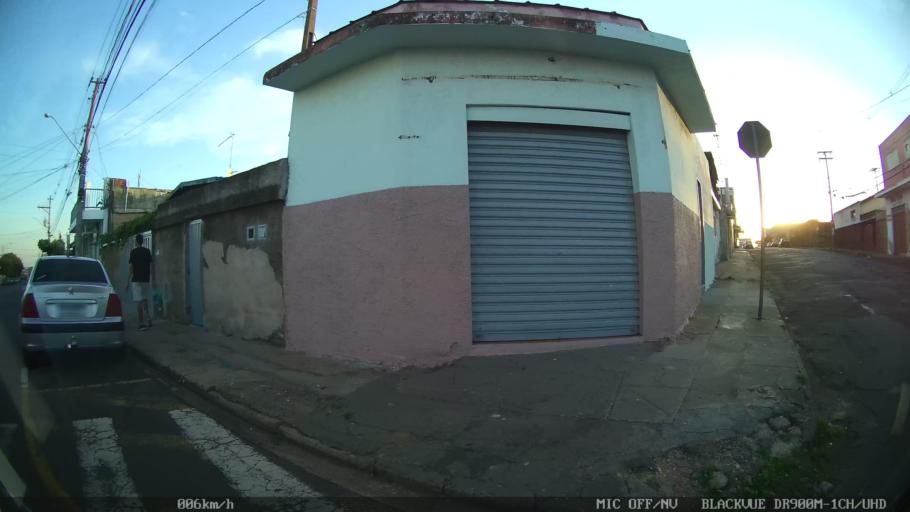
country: BR
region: Sao Paulo
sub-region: Franca
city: Franca
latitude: -20.5202
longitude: -47.4065
